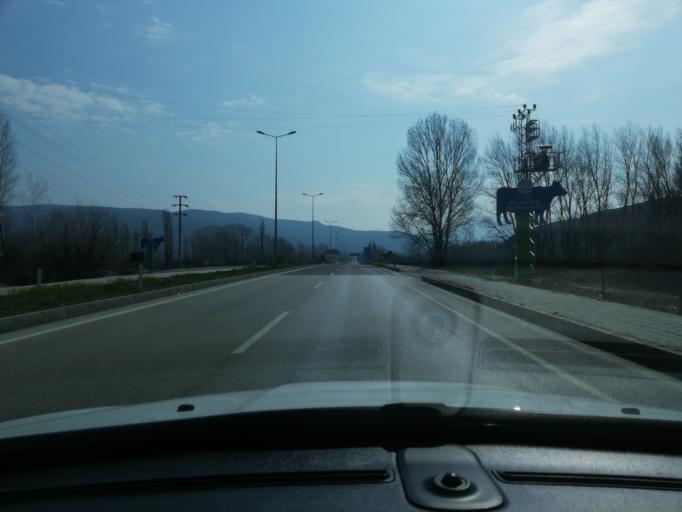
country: TR
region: Cankiri
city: Ilgaz
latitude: 40.9074
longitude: 33.6389
